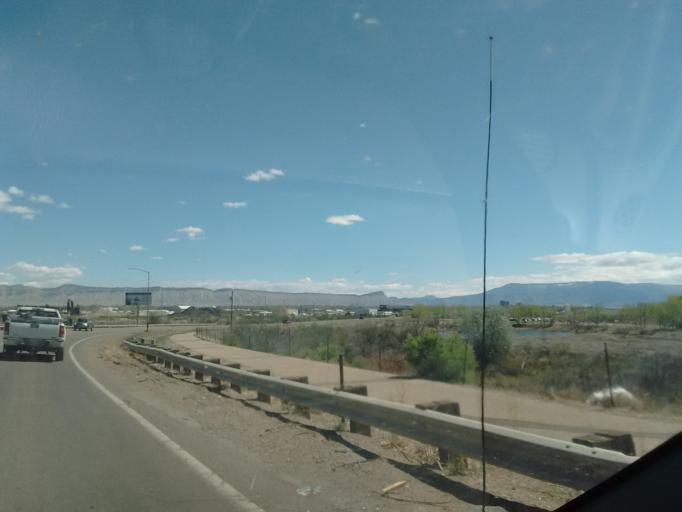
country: US
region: Colorado
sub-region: Mesa County
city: Redlands
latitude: 39.0893
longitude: -108.6237
